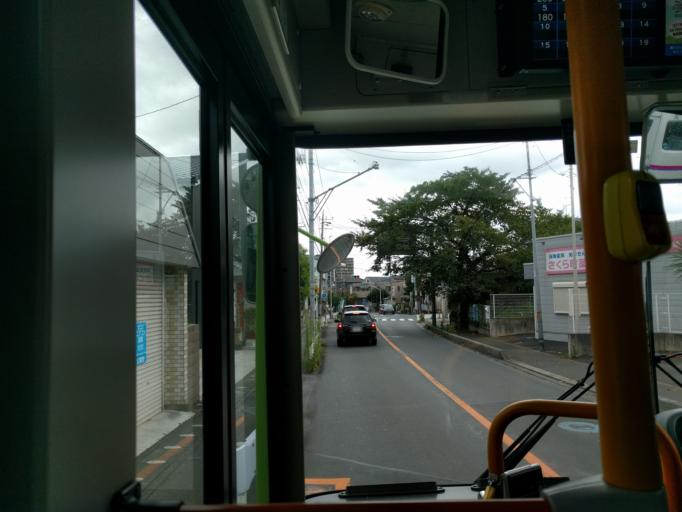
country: JP
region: Saitama
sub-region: Kawaguchi-shi
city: Hatogaya-honcho
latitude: 35.8384
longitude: 139.7390
